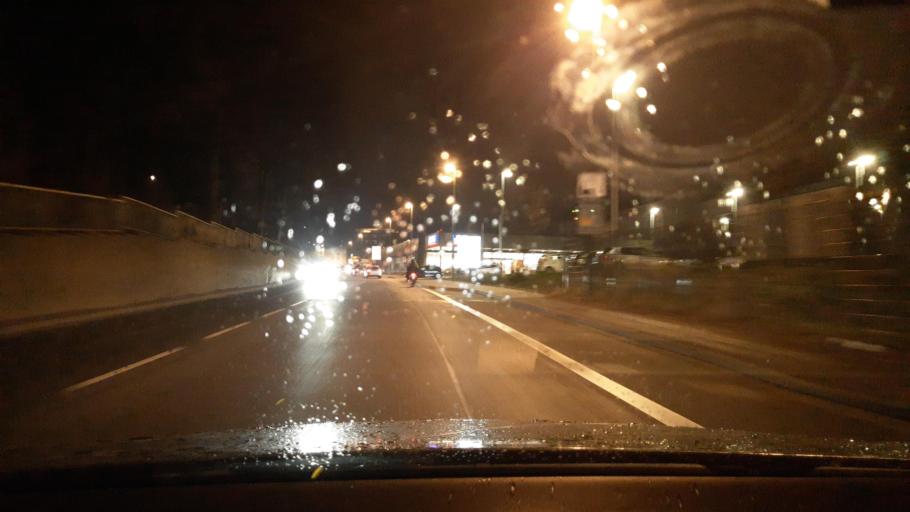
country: DE
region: North Rhine-Westphalia
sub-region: Regierungsbezirk Arnsberg
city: Luedenscheid
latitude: 51.2308
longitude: 7.6331
